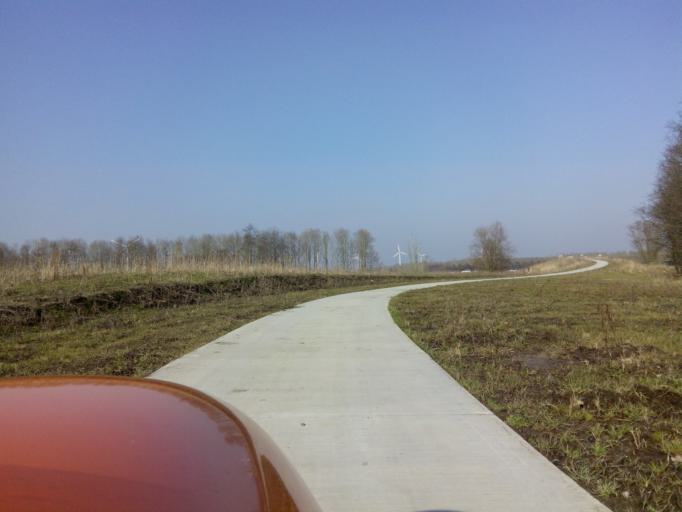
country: NL
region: Flevoland
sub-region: Gemeente Zeewolde
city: Zeewolde
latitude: 52.3226
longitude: 5.4488
